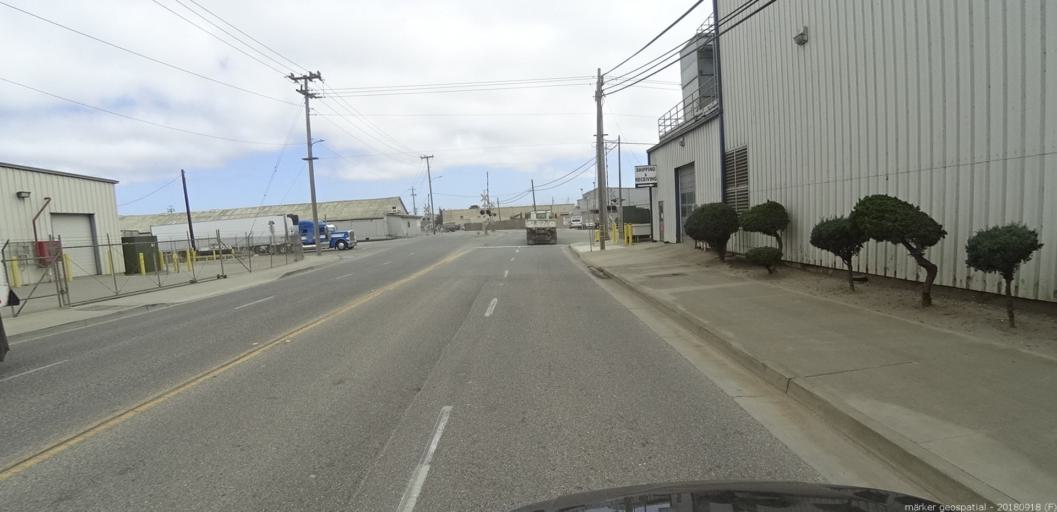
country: US
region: California
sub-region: Monterey County
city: Castroville
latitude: 36.7578
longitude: -121.7448
